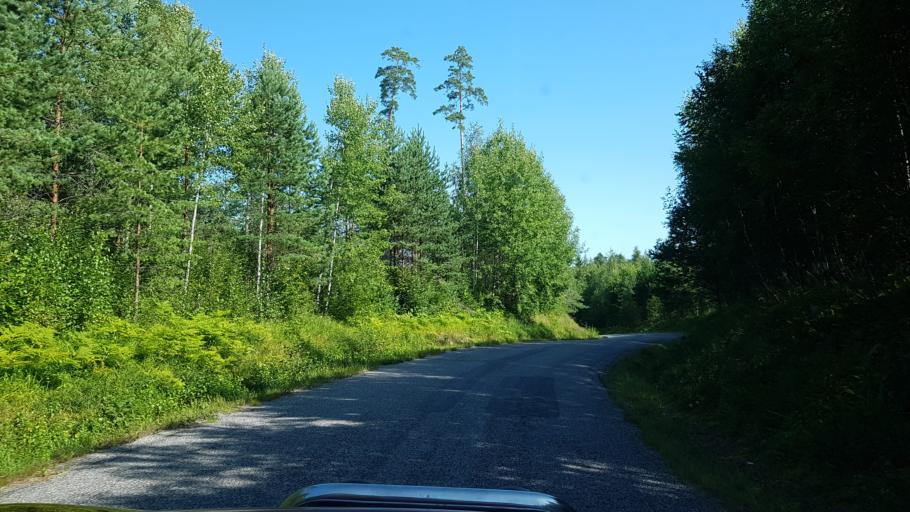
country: EE
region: Vorumaa
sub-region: Voru linn
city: Voru
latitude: 57.7166
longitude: 27.1978
